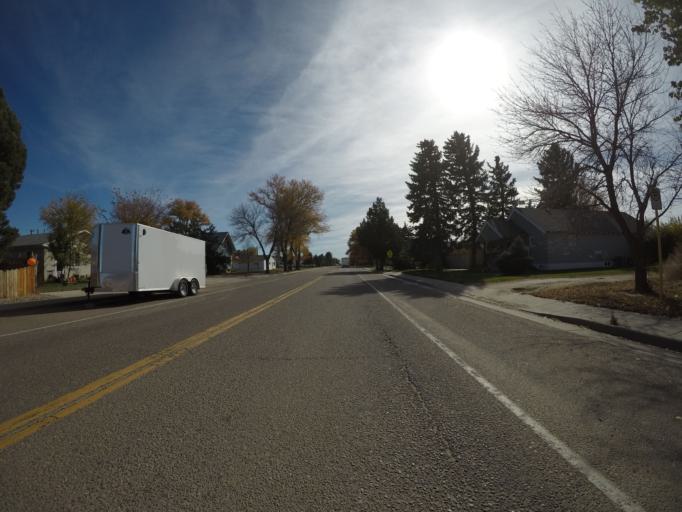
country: US
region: Colorado
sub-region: Kit Carson County
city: Burlington
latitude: 39.3067
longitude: -102.2602
